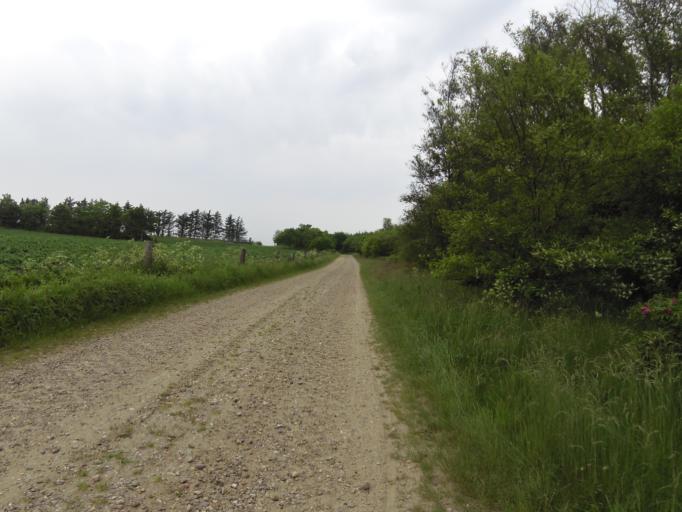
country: DK
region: South Denmark
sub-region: Esbjerg Kommune
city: Ribe
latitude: 55.3198
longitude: 8.8445
